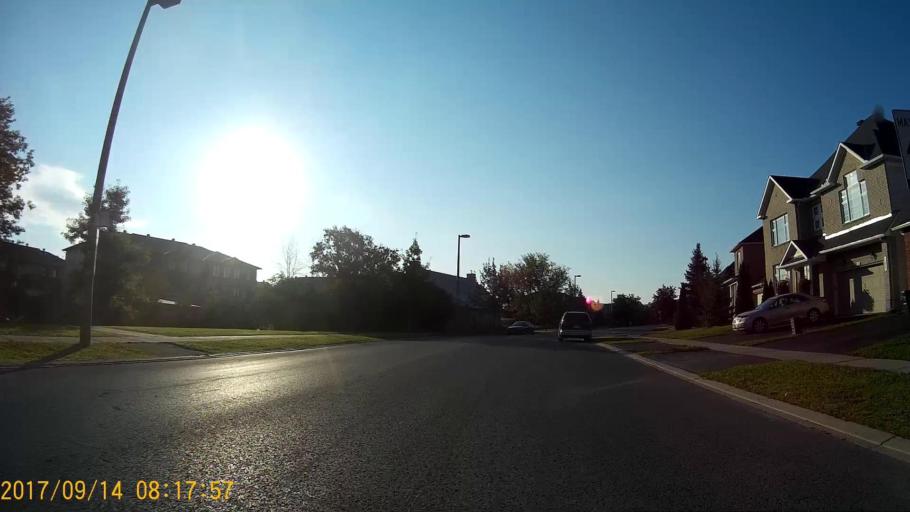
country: CA
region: Ontario
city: Bells Corners
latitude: 45.3534
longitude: -75.9347
